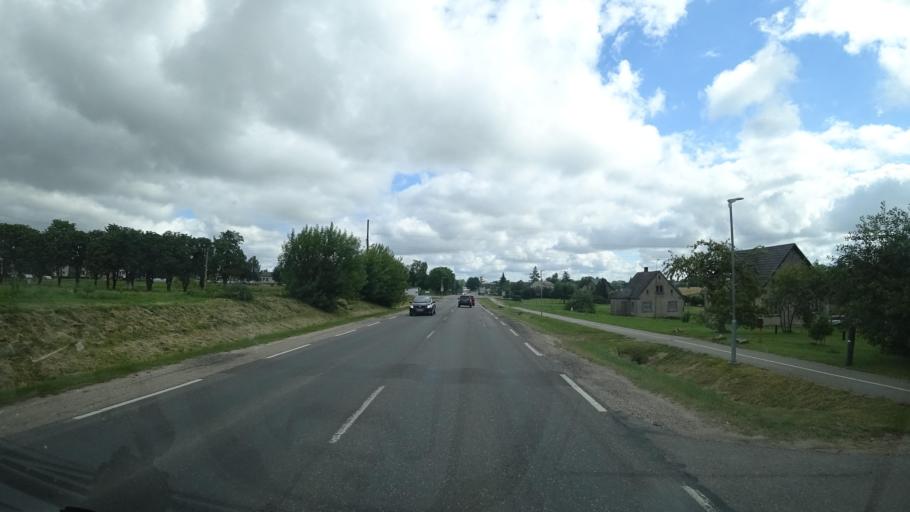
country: LT
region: Marijampoles apskritis
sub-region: Marijampole Municipality
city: Marijampole
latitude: 54.5326
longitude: 23.3335
